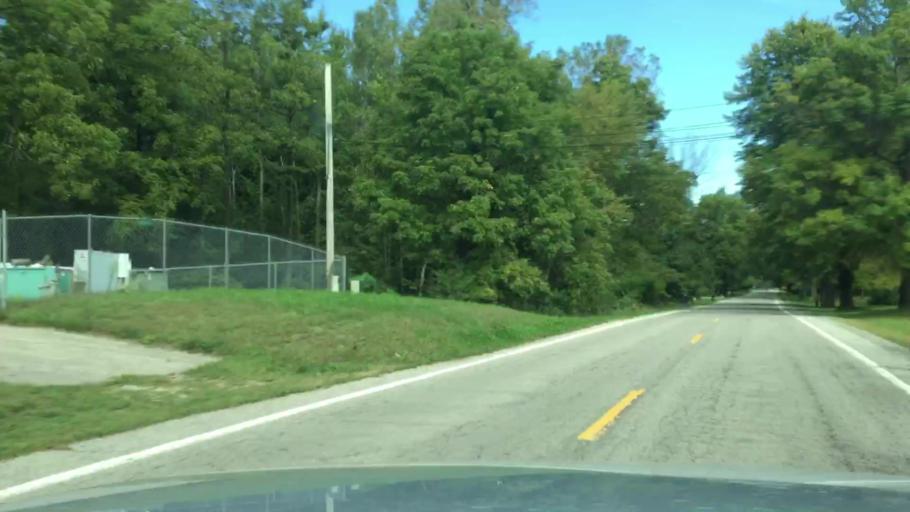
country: US
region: Michigan
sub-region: Wayne County
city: Belleville
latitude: 42.1528
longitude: -83.4612
